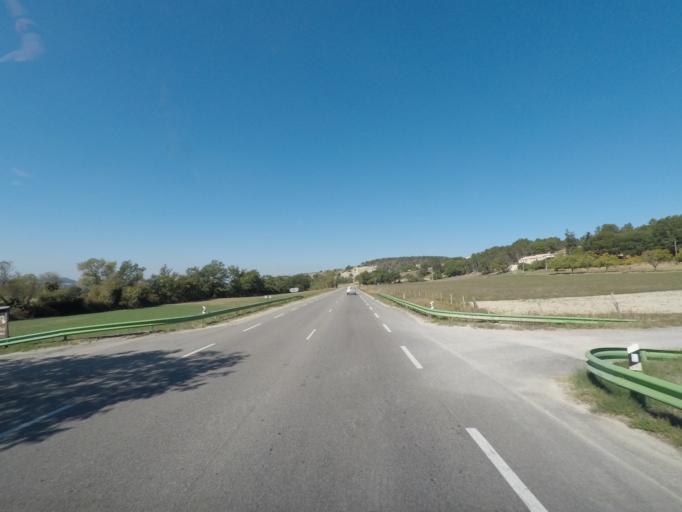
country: FR
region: Rhone-Alpes
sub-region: Departement de la Drome
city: Aouste-sur-Sye
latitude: 44.7009
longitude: 5.1232
